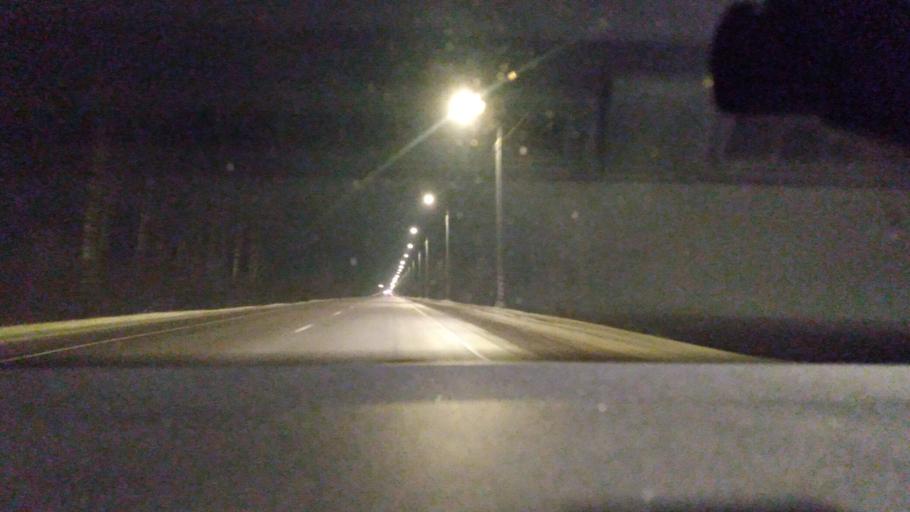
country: RU
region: Moskovskaya
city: Yegor'yevsk
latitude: 55.4520
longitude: 39.0016
